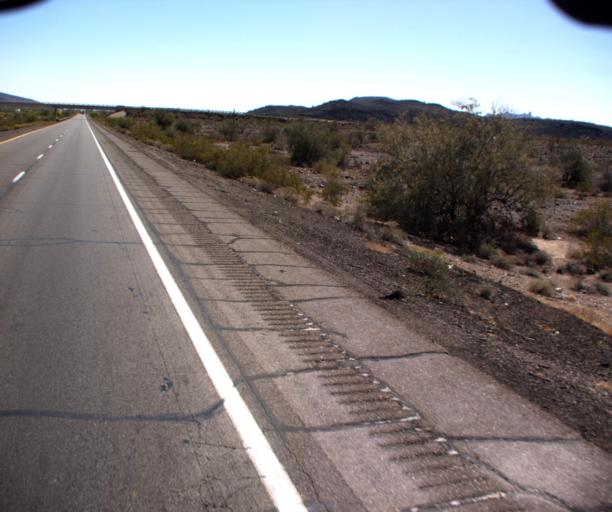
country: US
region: Arizona
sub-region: La Paz County
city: Quartzsite
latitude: 33.6564
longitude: -113.9691
